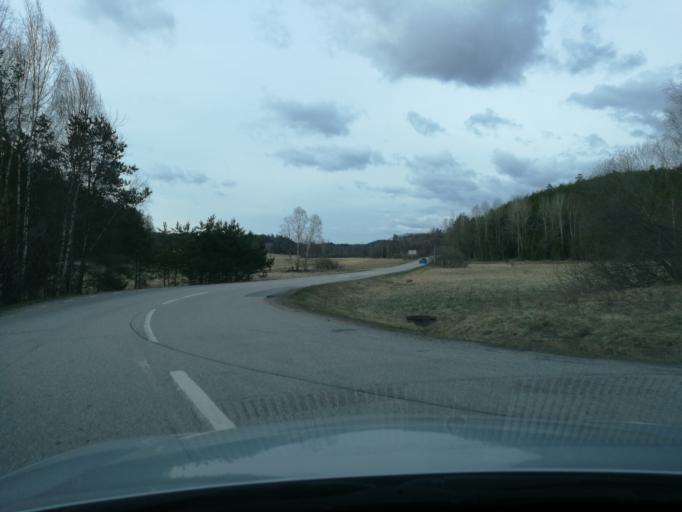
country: SE
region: Soedermanland
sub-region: Gnesta Kommun
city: Gnesta
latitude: 58.9091
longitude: 17.3297
